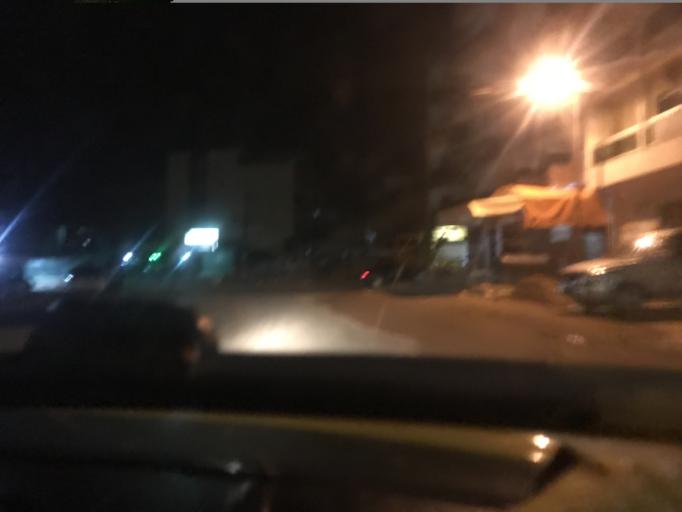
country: SN
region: Dakar
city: Grand Dakar
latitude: 14.7484
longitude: -17.4533
